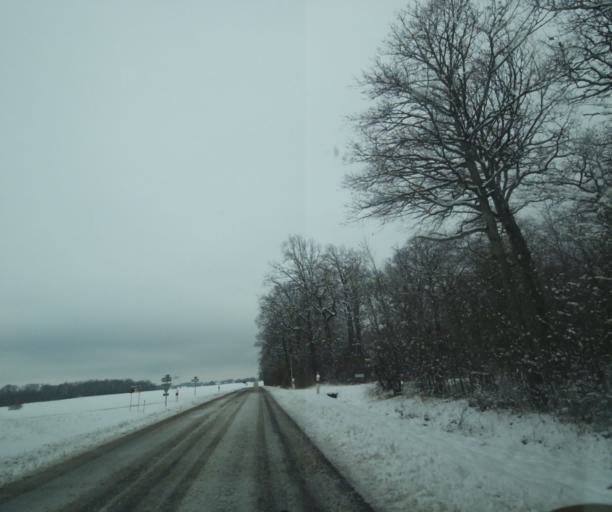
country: FR
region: Champagne-Ardenne
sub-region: Departement de la Haute-Marne
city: Montier-en-Der
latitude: 48.5298
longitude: 4.7492
